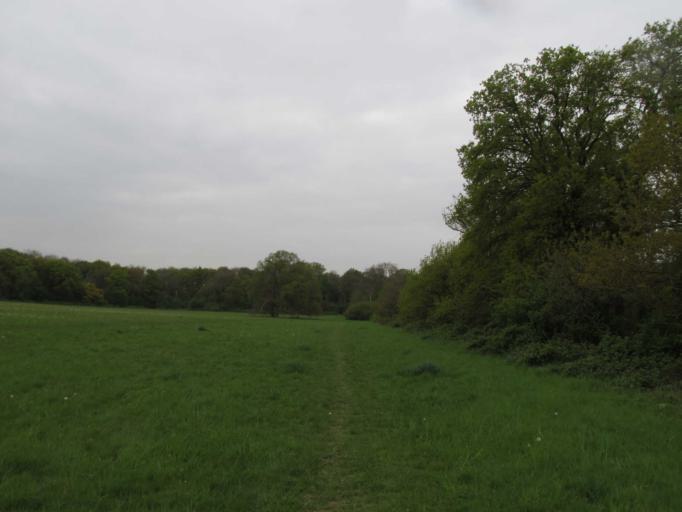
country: GB
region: England
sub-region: Royal Borough of Windsor and Maidenhead
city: Bisham
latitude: 51.5506
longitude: -0.7586
